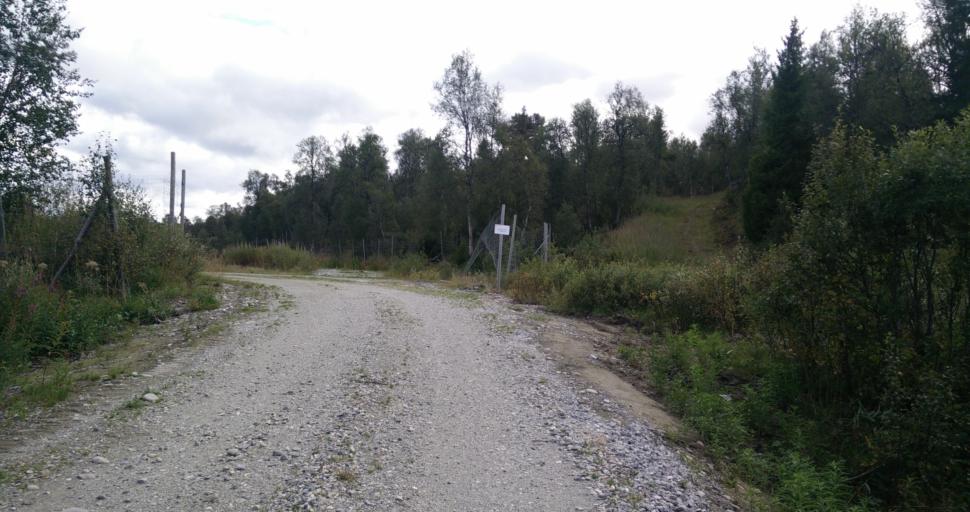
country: NO
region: Sor-Trondelag
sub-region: Tydal
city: Aas
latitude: 62.6340
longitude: 12.4187
